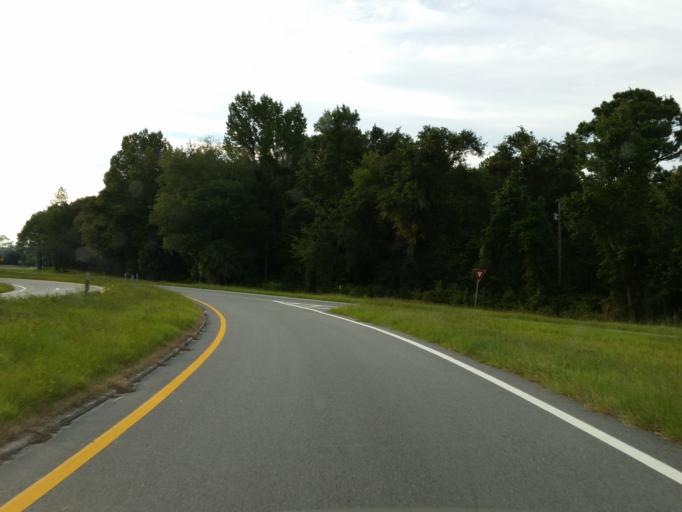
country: US
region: Georgia
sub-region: Echols County
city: Statenville
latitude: 30.5961
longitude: -83.1184
